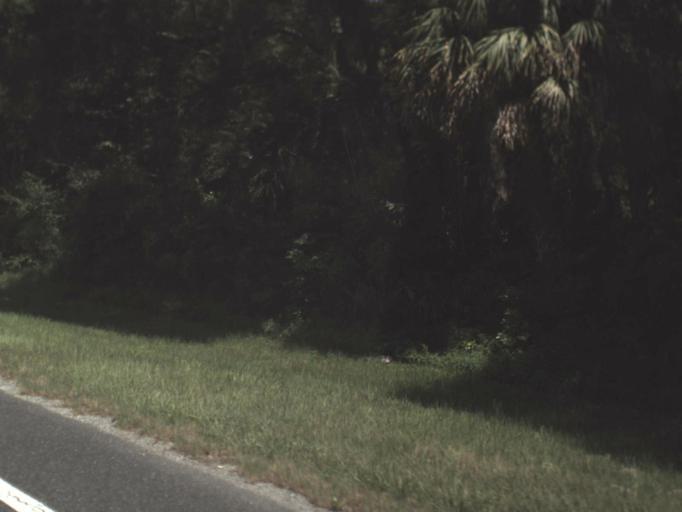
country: US
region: Florida
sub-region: Dixie County
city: Cross City
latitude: 29.6029
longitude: -83.0193
